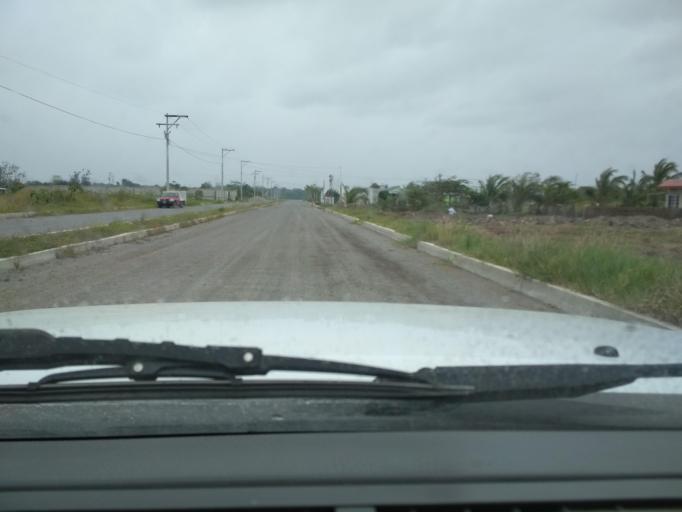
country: MX
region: Veracruz
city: Paso del Toro
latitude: 19.0431
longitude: -96.1344
